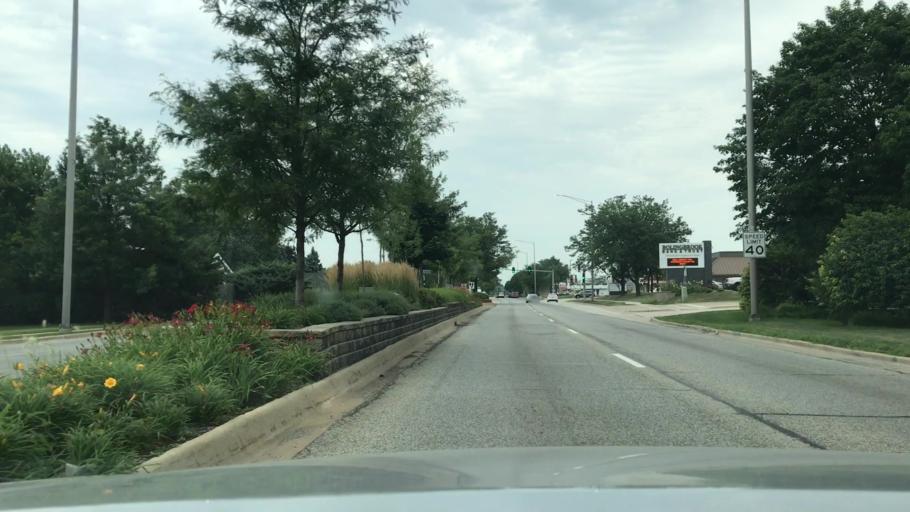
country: US
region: Illinois
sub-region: Will County
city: Bolingbrook
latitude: 41.6945
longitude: -88.0681
